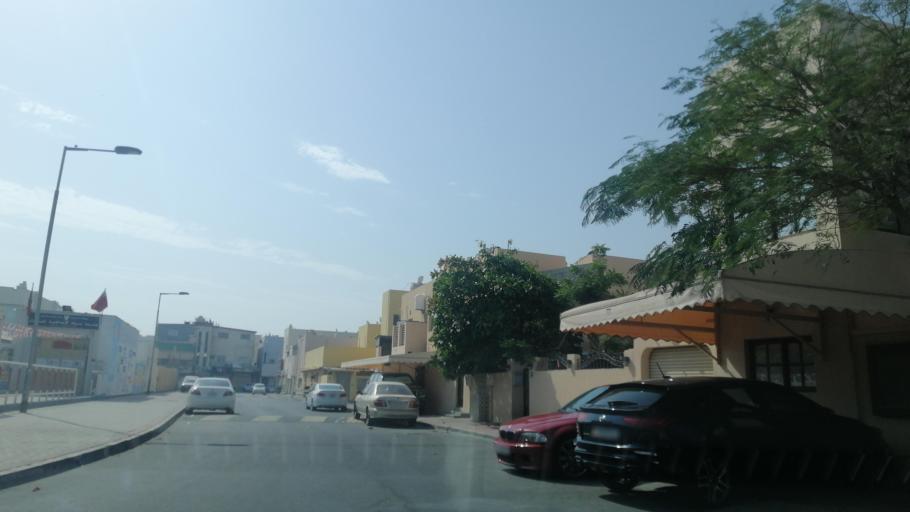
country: BH
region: Muharraq
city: Al Muharraq
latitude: 26.2560
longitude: 50.6294
